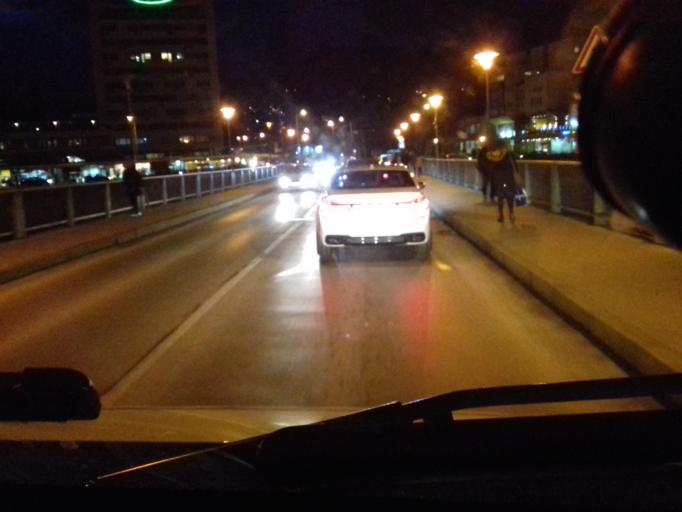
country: BA
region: Federation of Bosnia and Herzegovina
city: Zenica
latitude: 44.2035
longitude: 17.9090
